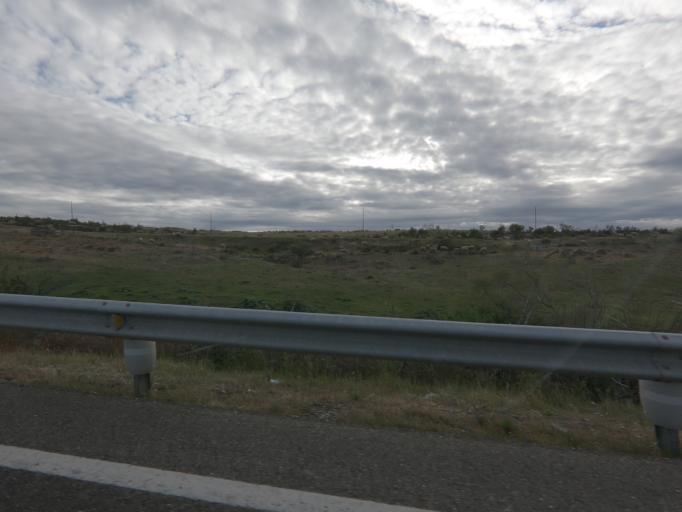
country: ES
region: Extremadura
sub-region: Provincia de Caceres
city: Torrejoncillo
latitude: 39.9381
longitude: -6.5064
